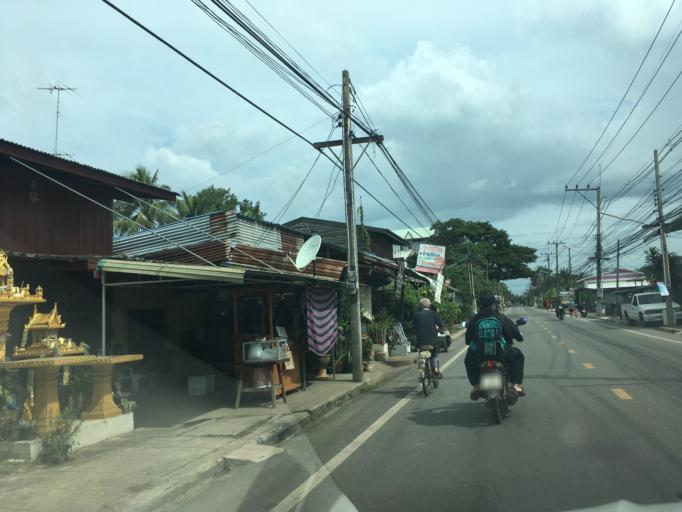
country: TH
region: Chachoengsao
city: Bang Khla
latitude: 13.7308
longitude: 101.2108
